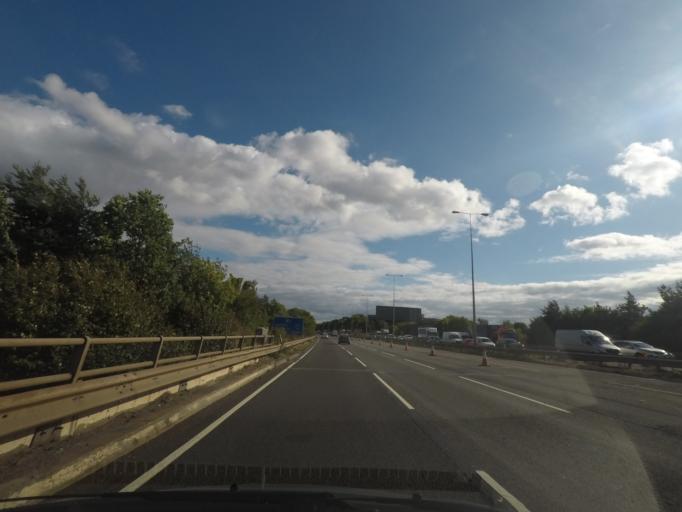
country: GB
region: England
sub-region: Leicestershire
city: Kegworth
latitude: 52.8102
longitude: -1.3056
